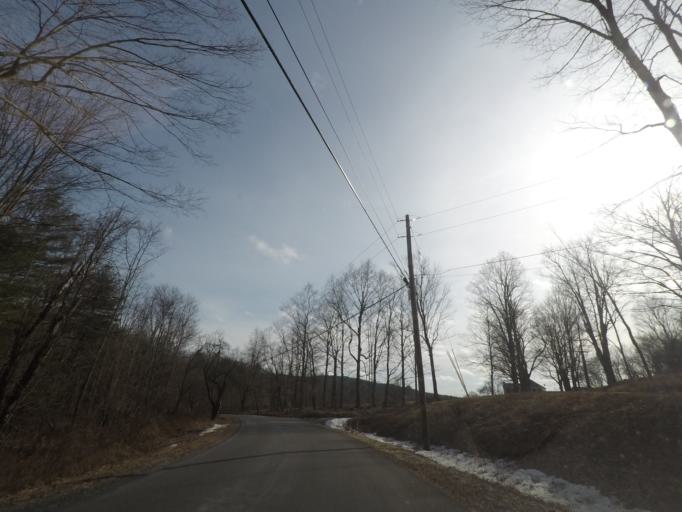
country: US
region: New York
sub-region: Rensselaer County
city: Nassau
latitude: 42.5051
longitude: -73.5529
